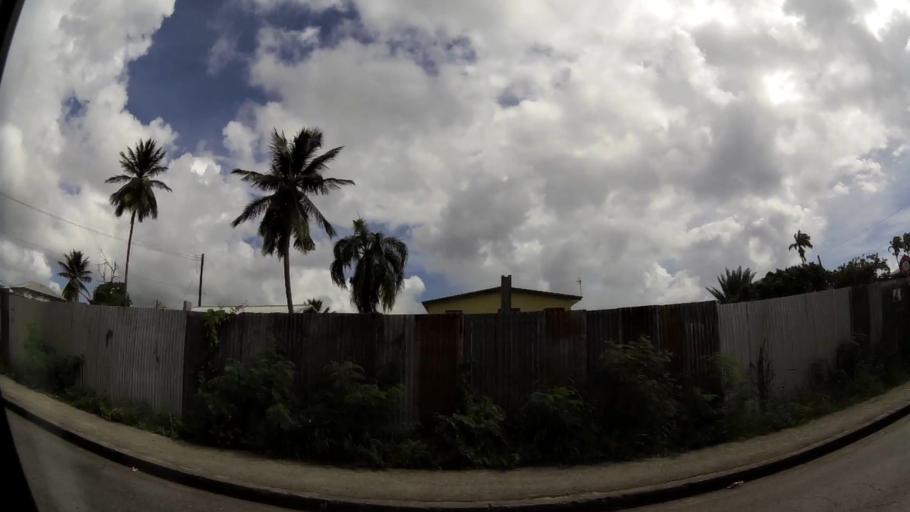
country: BB
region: Saint Michael
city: Bridgetown
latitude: 13.1085
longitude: -59.6192
